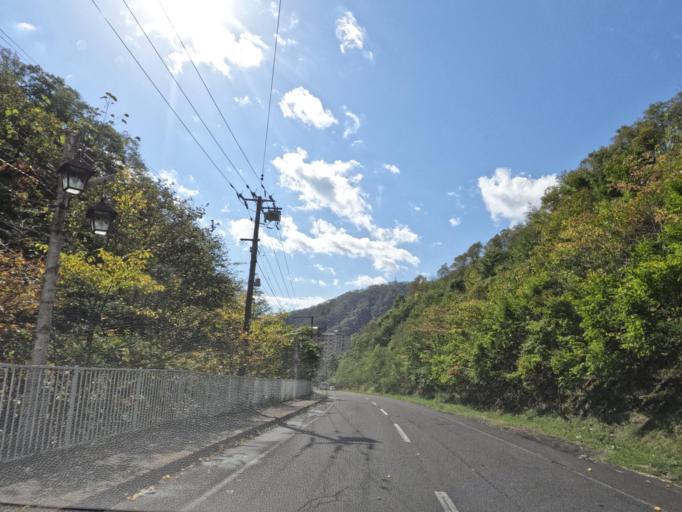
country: JP
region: Hokkaido
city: Shiraoi
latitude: 42.4990
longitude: 141.1414
